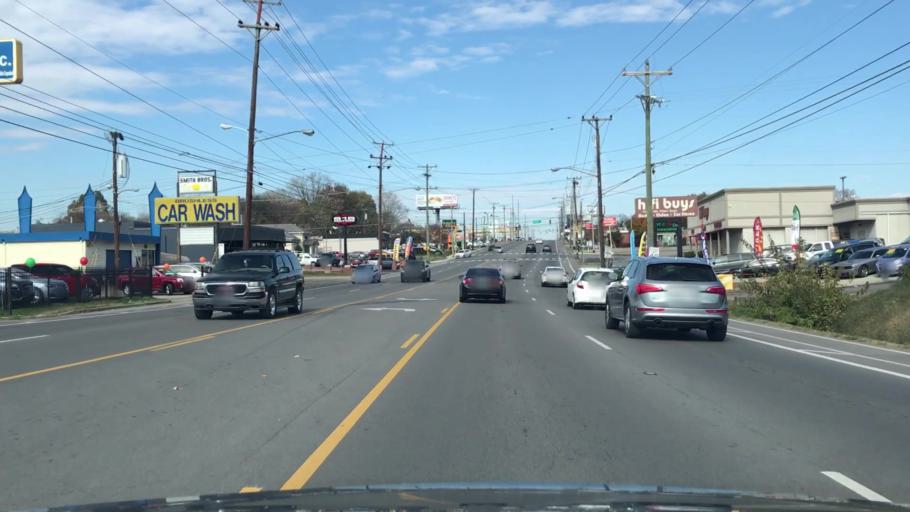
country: US
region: Tennessee
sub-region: Davidson County
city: Oak Hill
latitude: 36.0921
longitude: -86.7355
